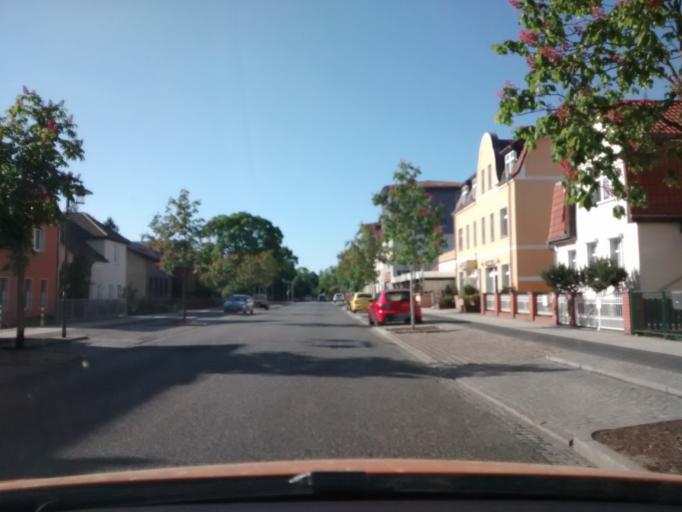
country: DE
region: Brandenburg
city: Furstenwalde
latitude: 52.3501
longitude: 14.0690
